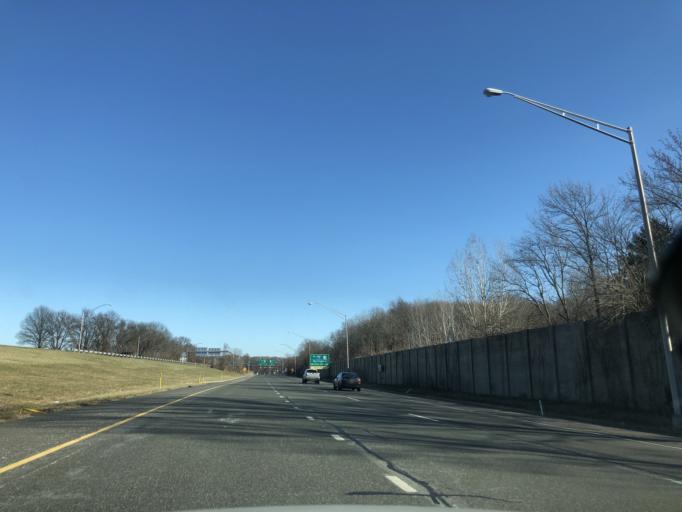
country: US
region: Pennsylvania
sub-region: Bucks County
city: Croydon
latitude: 40.1109
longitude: -74.8879
